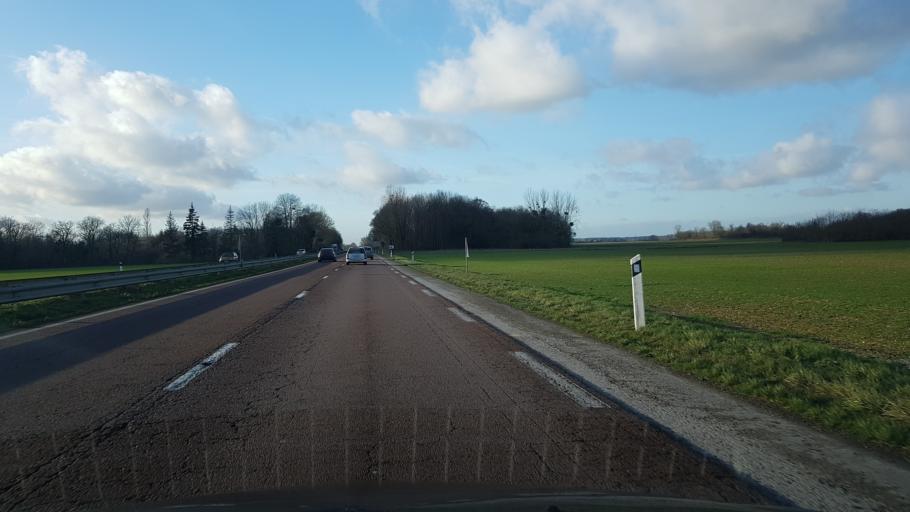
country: FR
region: Champagne-Ardenne
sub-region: Departement de la Haute-Marne
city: Villiers-en-Lieu
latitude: 48.6504
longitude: 4.8501
